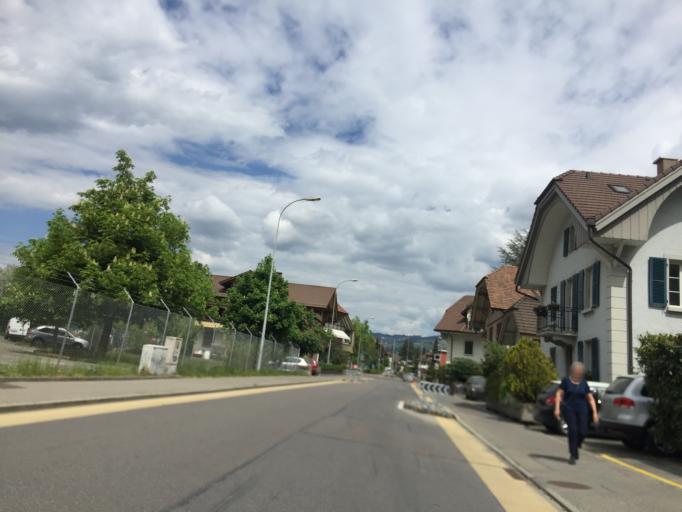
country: CH
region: Bern
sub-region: Thun District
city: Thun
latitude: 46.7631
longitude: 7.6203
